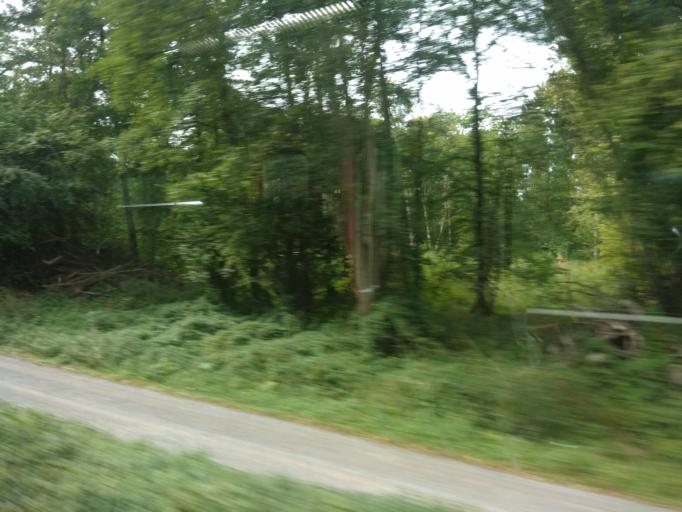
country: DE
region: Baden-Wuerttemberg
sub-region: Karlsruhe Region
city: Weingarten
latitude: 49.0397
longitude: 8.5027
